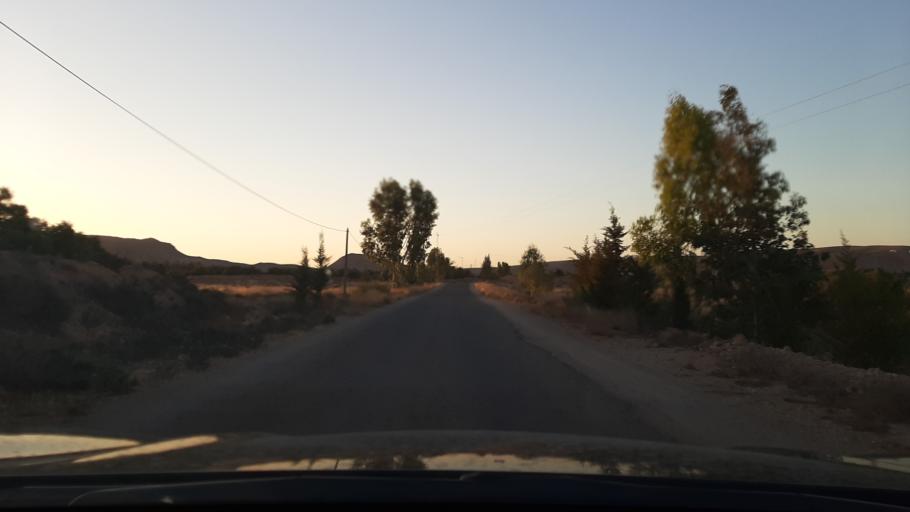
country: TN
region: Qabis
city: Matmata
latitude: 33.5632
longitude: 10.1804
